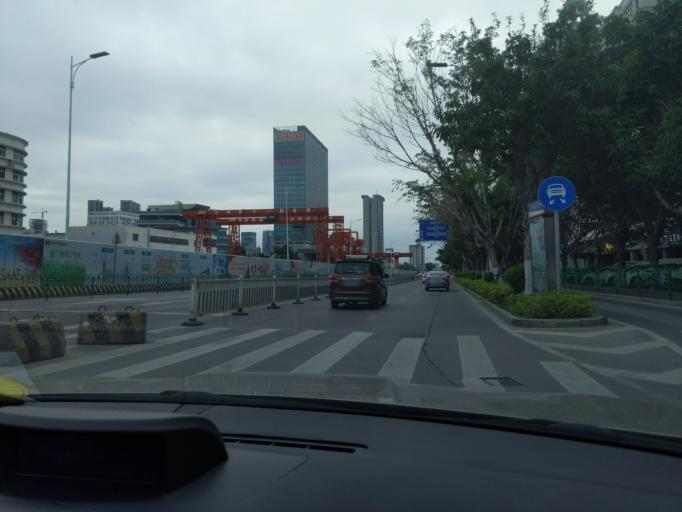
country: CN
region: Fujian
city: Liuwudian
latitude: 24.4859
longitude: 118.1722
